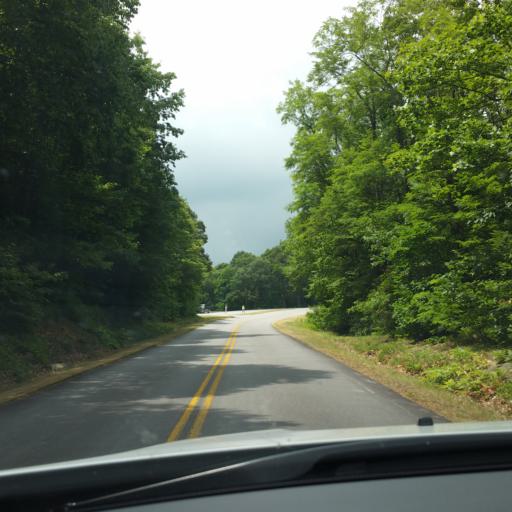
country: US
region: North Carolina
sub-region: Buncombe County
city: Bent Creek
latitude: 35.4442
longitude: -82.7193
